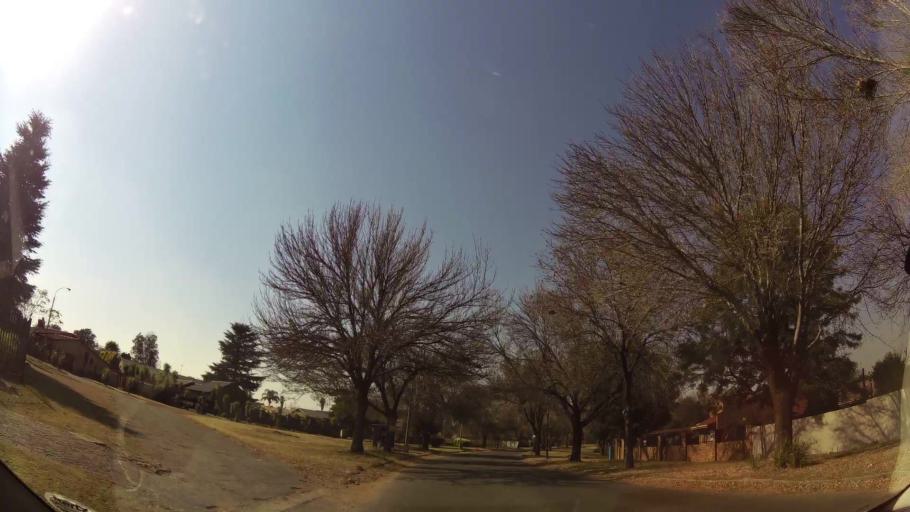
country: ZA
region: Gauteng
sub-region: Ekurhuleni Metropolitan Municipality
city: Boksburg
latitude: -26.1587
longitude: 28.2661
